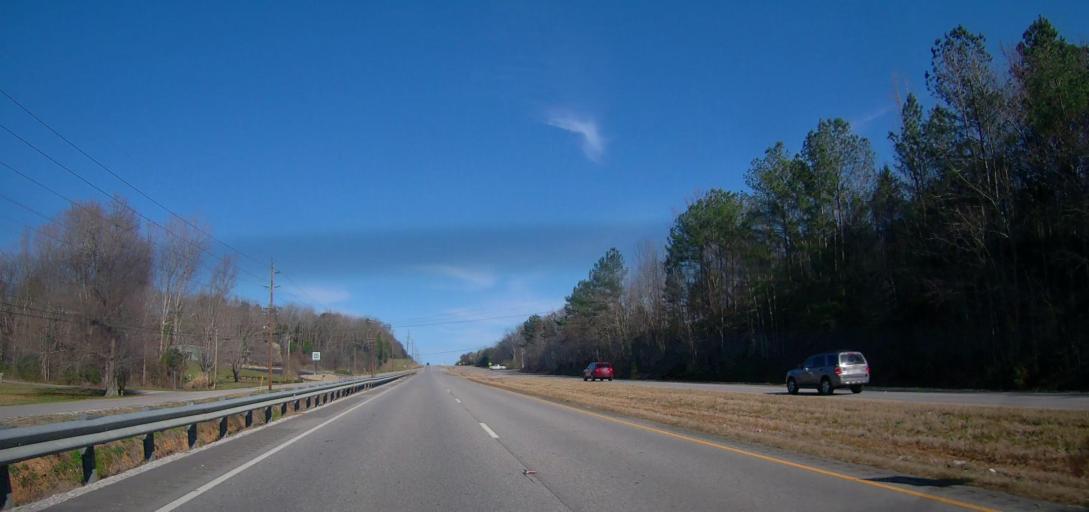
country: US
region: Alabama
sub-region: Lauderdale County
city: Killen
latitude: 34.8598
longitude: -87.5081
